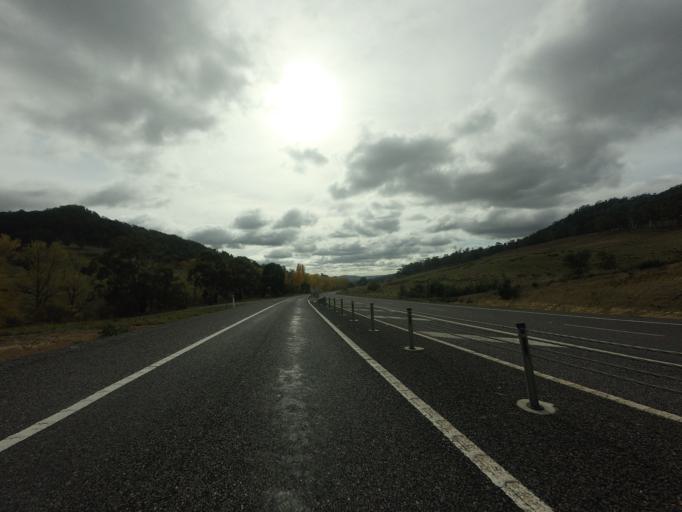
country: AU
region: Tasmania
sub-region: Brighton
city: Bridgewater
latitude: -42.5653
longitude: 147.2086
